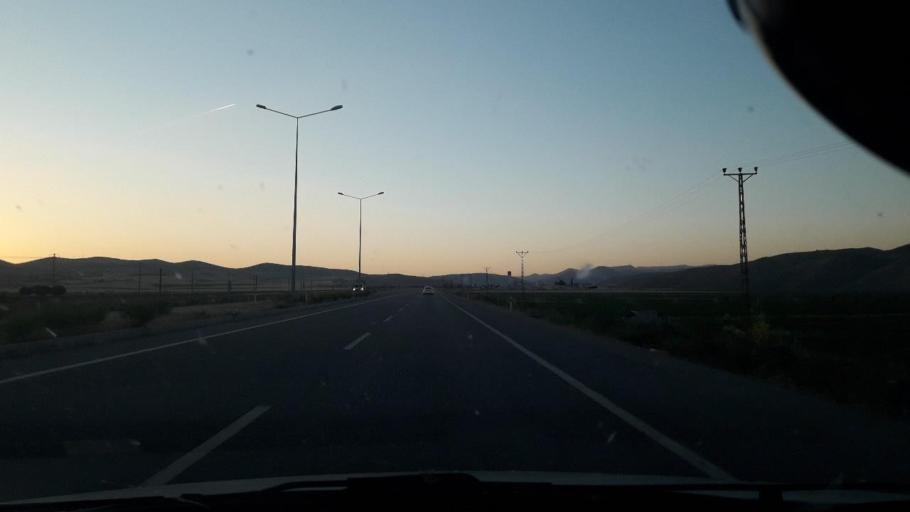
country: TR
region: Malatya
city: Yazihan
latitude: 38.6050
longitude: 38.1786
